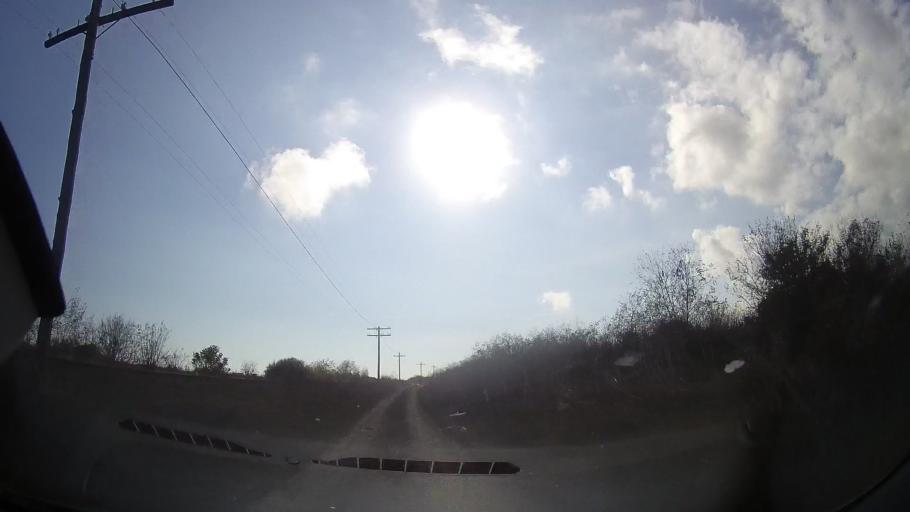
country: RO
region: Constanta
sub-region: Comuna Tuzla
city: Tuzla
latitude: 43.9897
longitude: 28.6450
